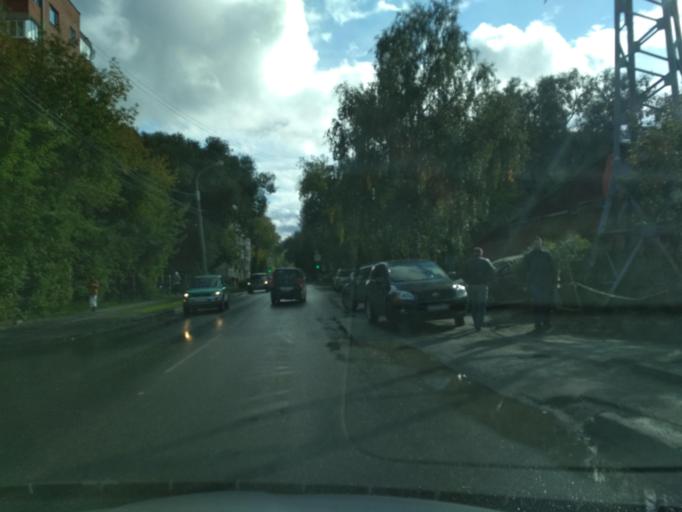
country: RU
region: Tomsk
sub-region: Tomskiy Rayon
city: Tomsk
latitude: 56.4700
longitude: 84.9756
